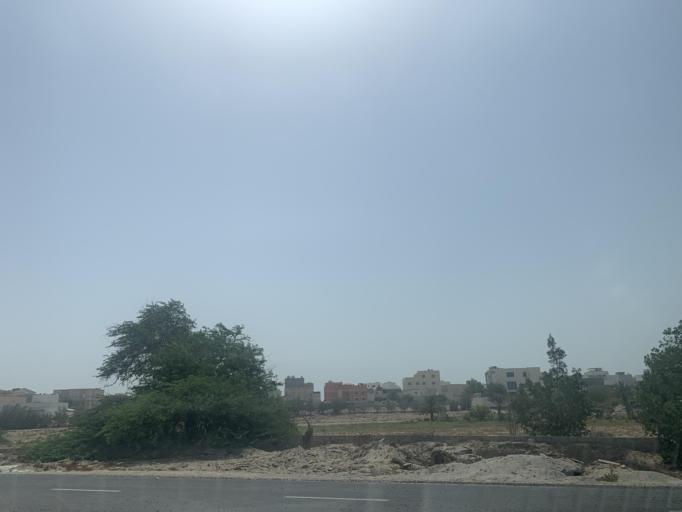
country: BH
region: Northern
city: Madinat `Isa
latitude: 26.1868
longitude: 50.4902
